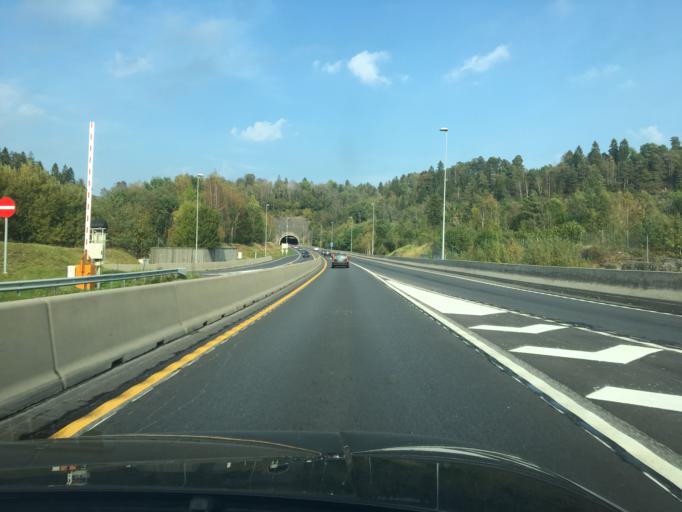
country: NO
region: Telemark
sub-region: Porsgrunn
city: Porsgrunn
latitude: 59.0770
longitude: 9.6640
